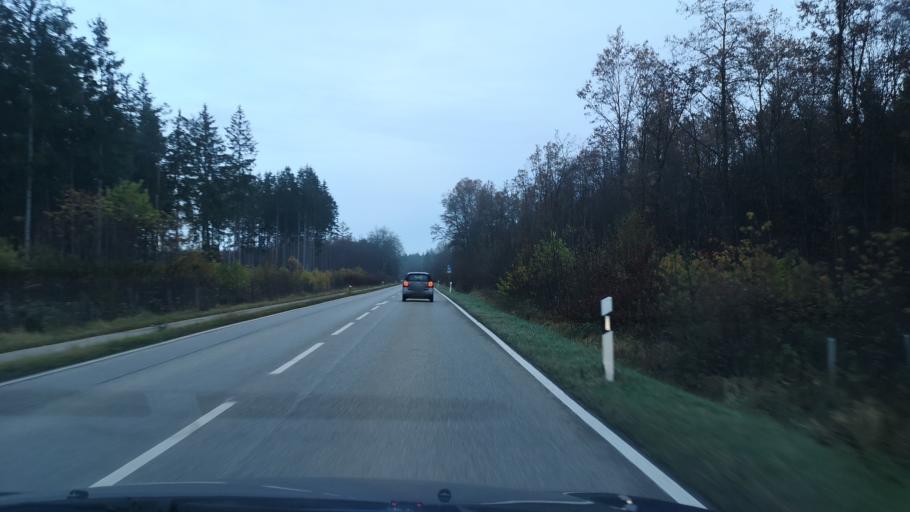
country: DE
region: Bavaria
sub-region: Upper Bavaria
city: Forstinning
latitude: 48.1389
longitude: 11.9286
